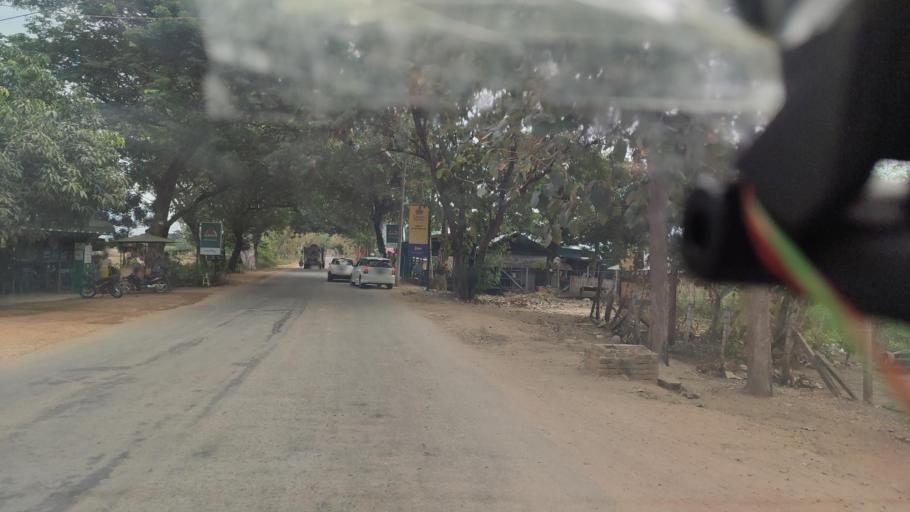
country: MM
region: Mandalay
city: Pyinmana
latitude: 19.7755
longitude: 96.2574
